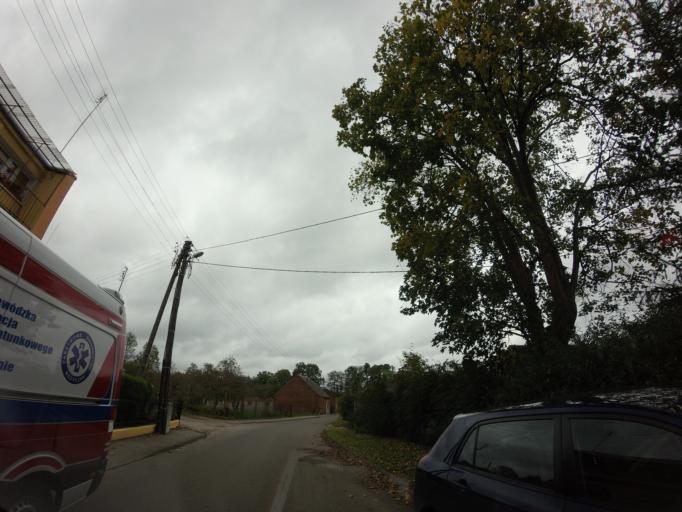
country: PL
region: West Pomeranian Voivodeship
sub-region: Powiat choszczenski
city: Drawno
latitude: 53.2151
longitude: 15.7641
